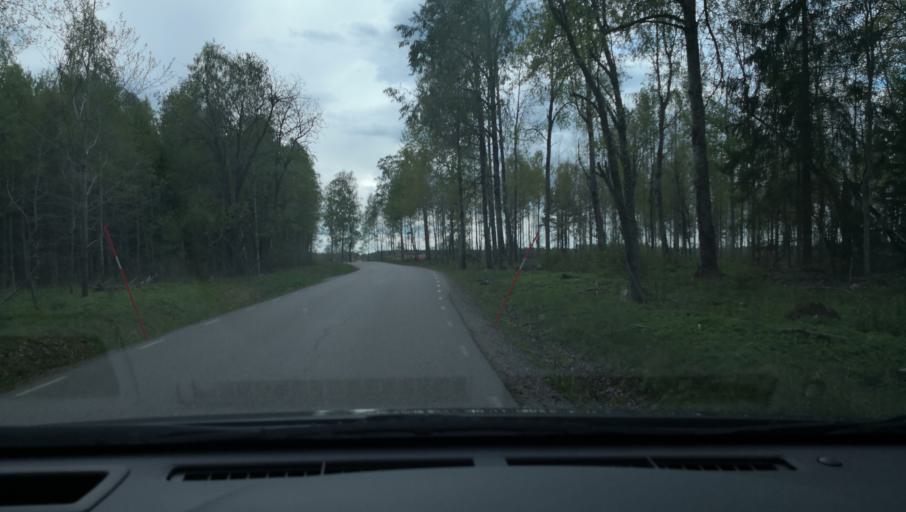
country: SE
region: OErebro
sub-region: Kumla Kommun
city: Hallabrottet
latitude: 59.1554
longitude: 15.1794
